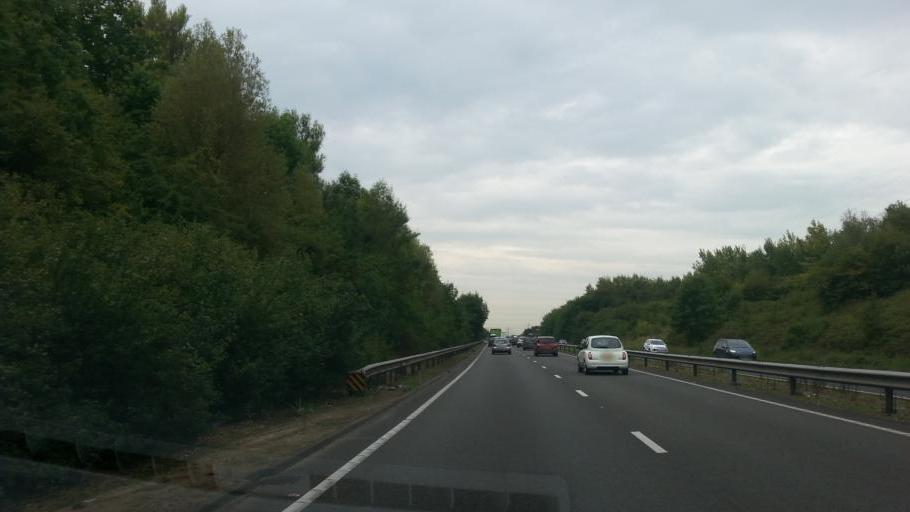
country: GB
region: England
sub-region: Cambridgeshire
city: Eaton Socon
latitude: 52.2162
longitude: -0.2988
